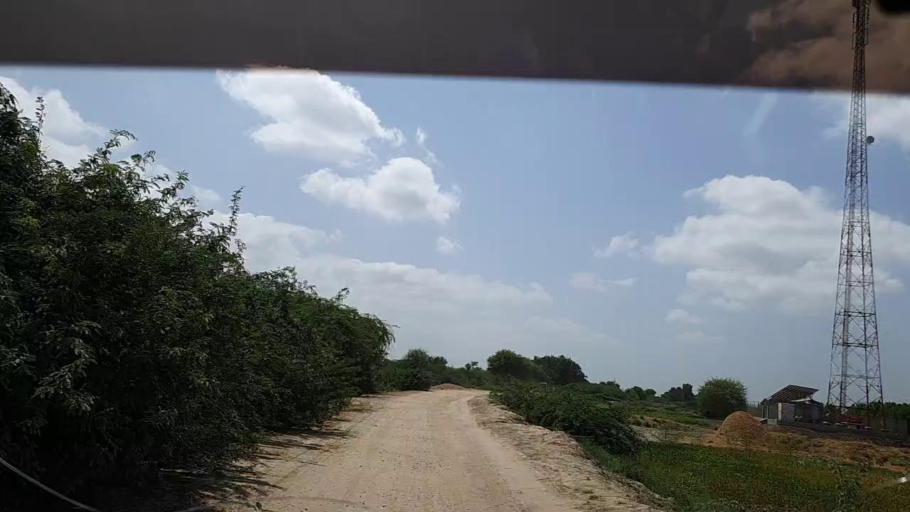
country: PK
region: Sindh
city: Badin
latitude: 24.5805
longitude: 68.7846
